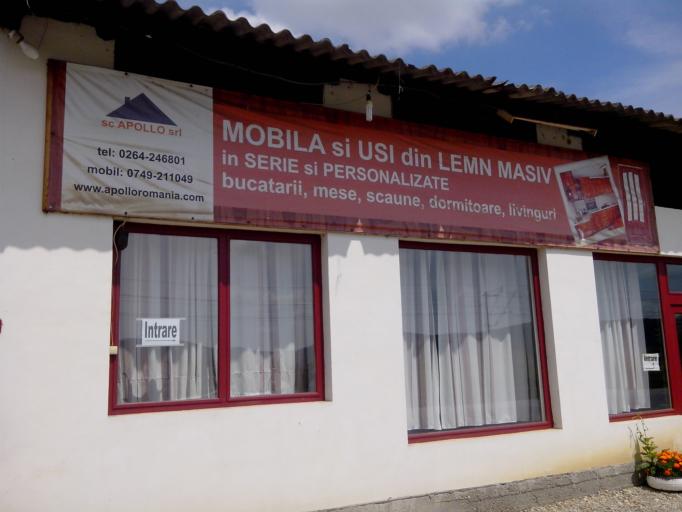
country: RO
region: Cluj
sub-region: Comuna Iclod
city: Iclod
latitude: 47.0068
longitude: 23.8462
